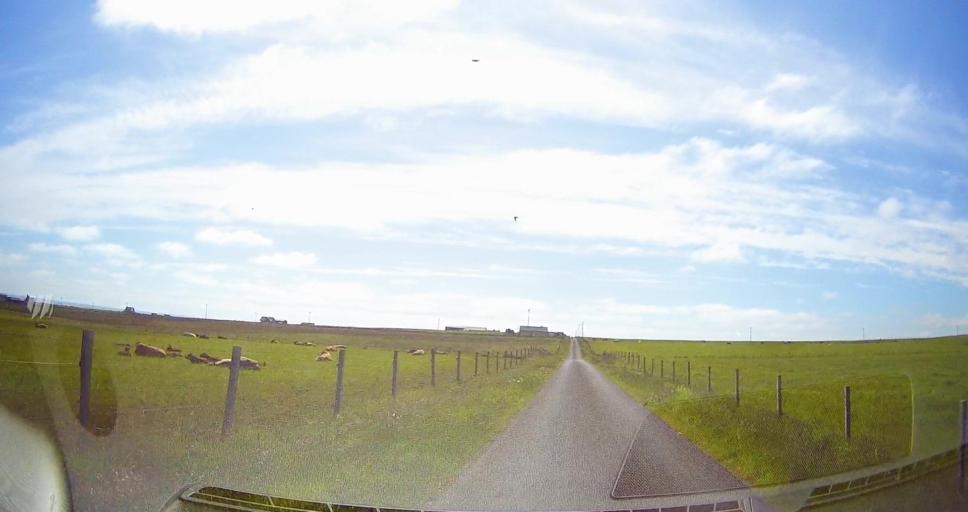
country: GB
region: Scotland
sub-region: Orkney Islands
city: Kirkwall
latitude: 58.8344
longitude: -2.9005
